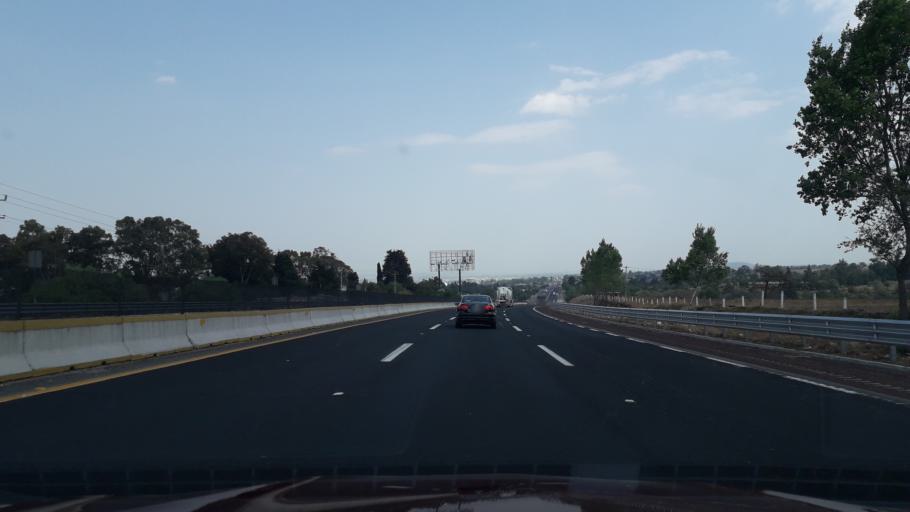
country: MX
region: Puebla
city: San Matias Tlalancaleca
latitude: 19.3203
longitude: -98.5133
